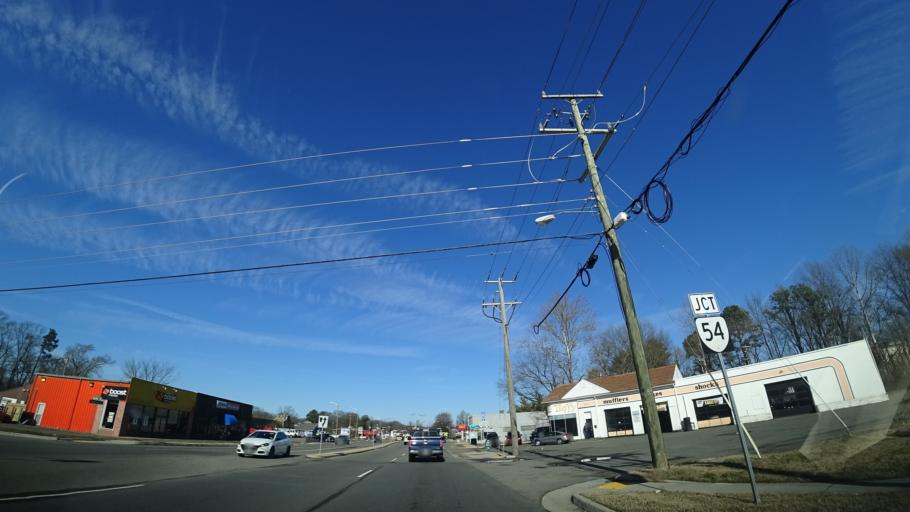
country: US
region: Virginia
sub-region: Hanover County
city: Ashland
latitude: 37.7566
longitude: -77.4714
